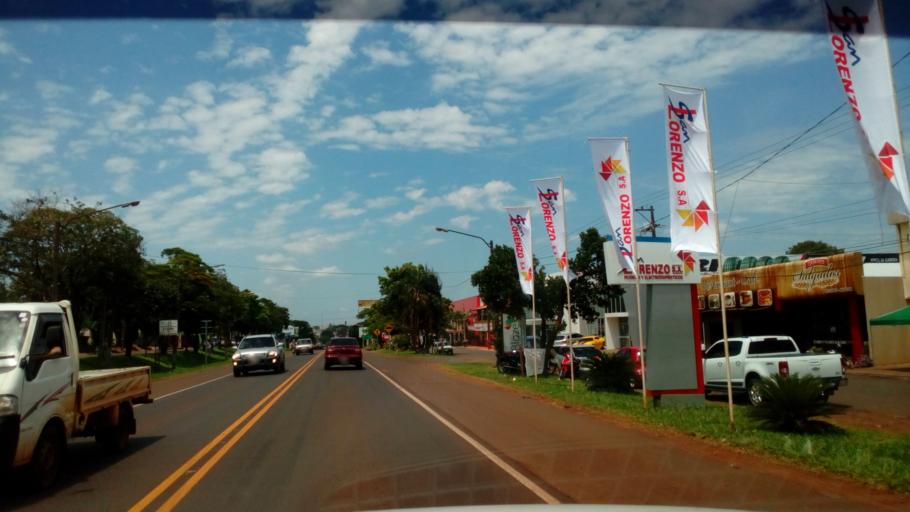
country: PY
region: Alto Parana
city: Santa Rita
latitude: -25.7846
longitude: -55.0804
